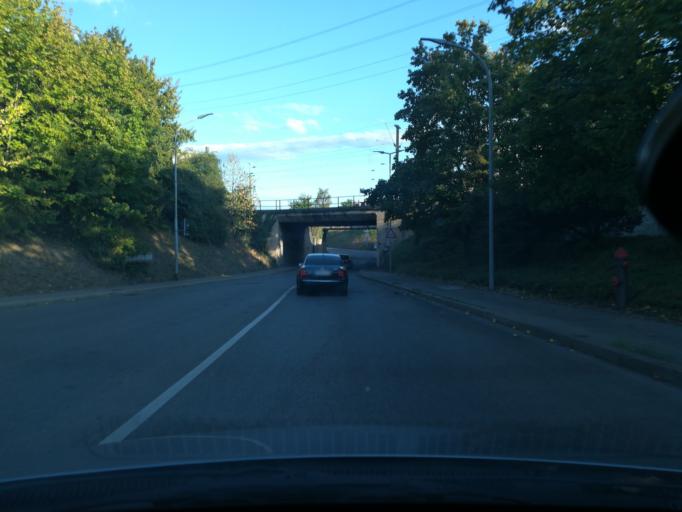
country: DE
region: Baden-Wuerttemberg
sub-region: Freiburg Region
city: Singen
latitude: 47.7615
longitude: 8.8496
